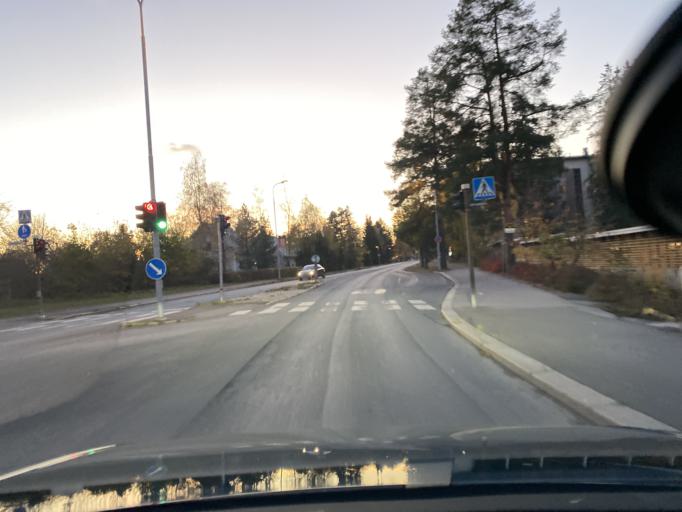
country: FI
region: Pirkanmaa
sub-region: Tampere
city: Tampere
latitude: 61.4700
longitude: 23.7489
